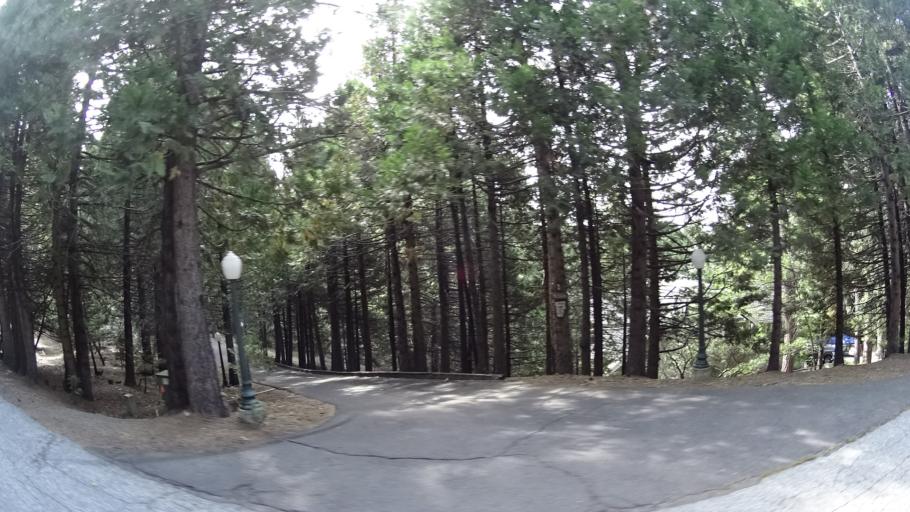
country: US
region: California
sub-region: Calaveras County
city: Arnold
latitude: 38.2559
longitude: -120.3372
